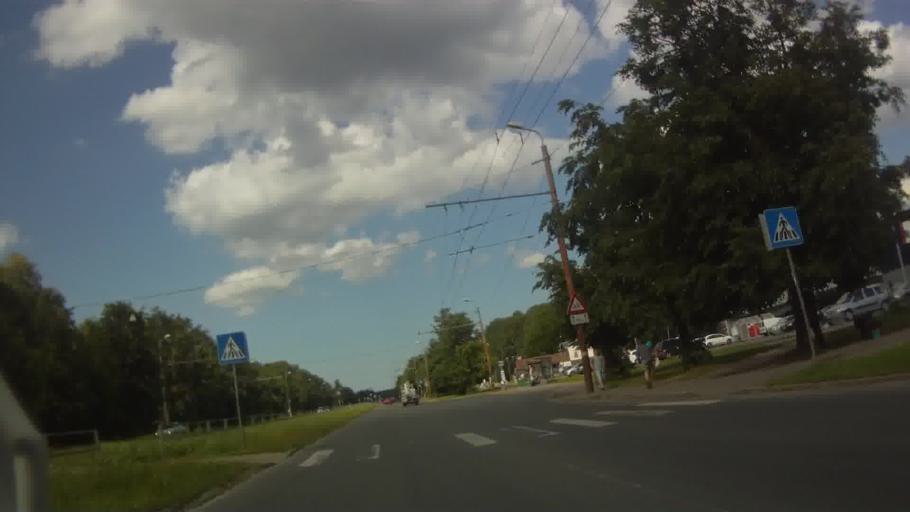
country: LV
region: Stopini
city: Ulbroka
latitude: 56.9415
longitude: 24.2051
